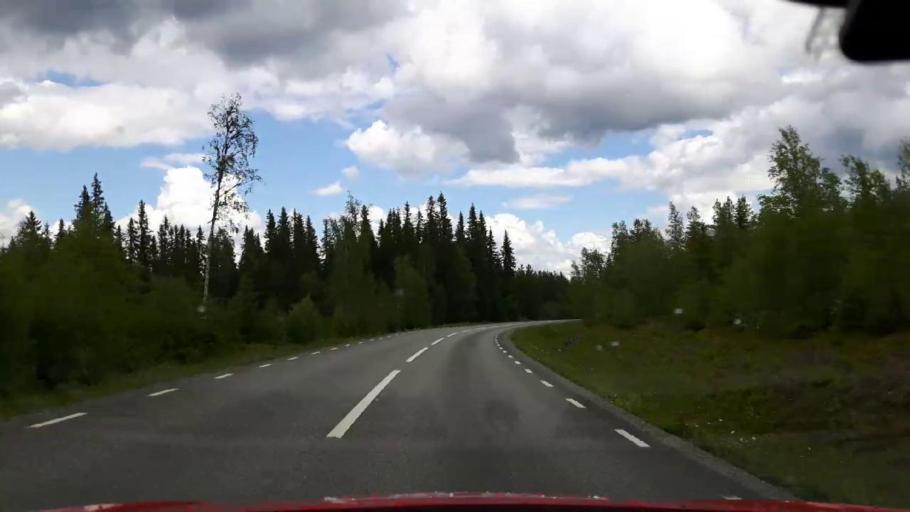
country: SE
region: Jaemtland
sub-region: Krokoms Kommun
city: Krokom
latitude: 63.7857
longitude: 14.3572
